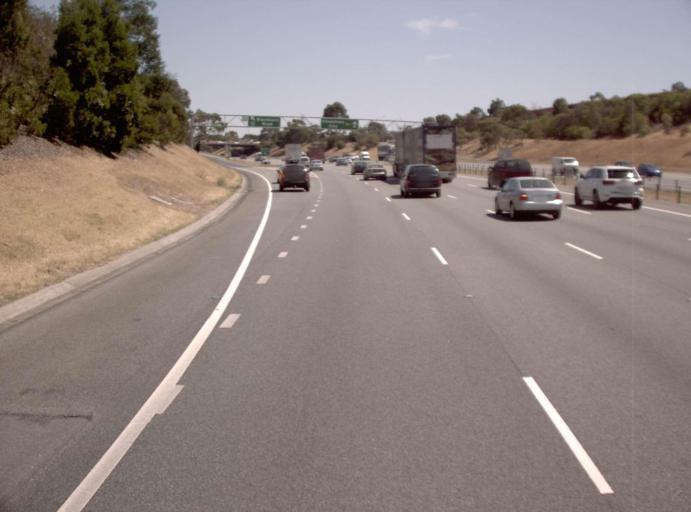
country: AU
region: Victoria
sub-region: Monash
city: Notting Hill
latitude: -37.8974
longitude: 145.1481
